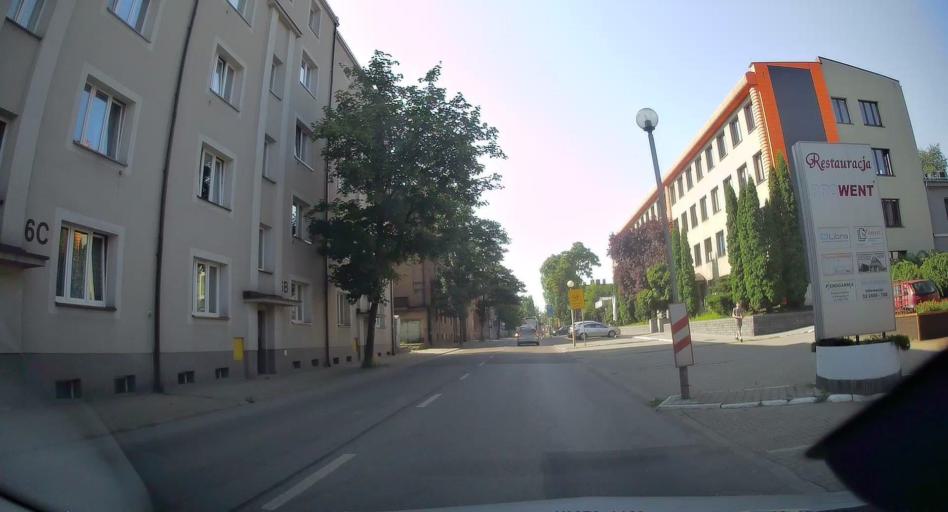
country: PL
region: Silesian Voivodeship
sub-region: Swietochlowice
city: Swietochlowice
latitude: 50.2892
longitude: 18.9142
